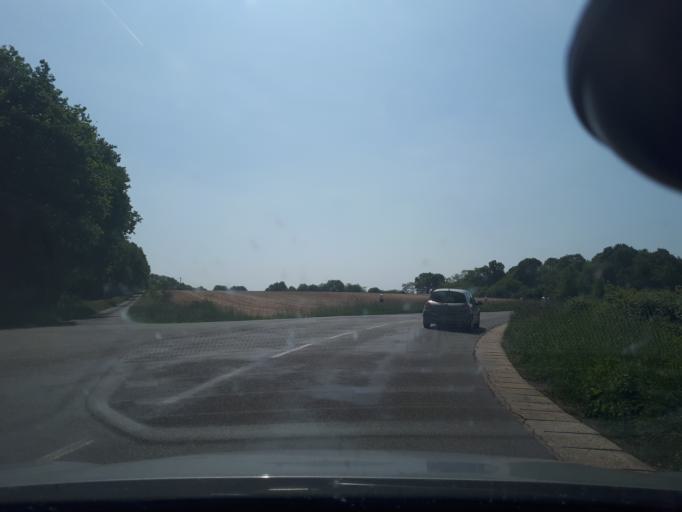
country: FR
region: Pays de la Loire
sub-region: Departement de la Sarthe
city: Le Breil-sur-Merize
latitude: 48.0248
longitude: 0.4525
